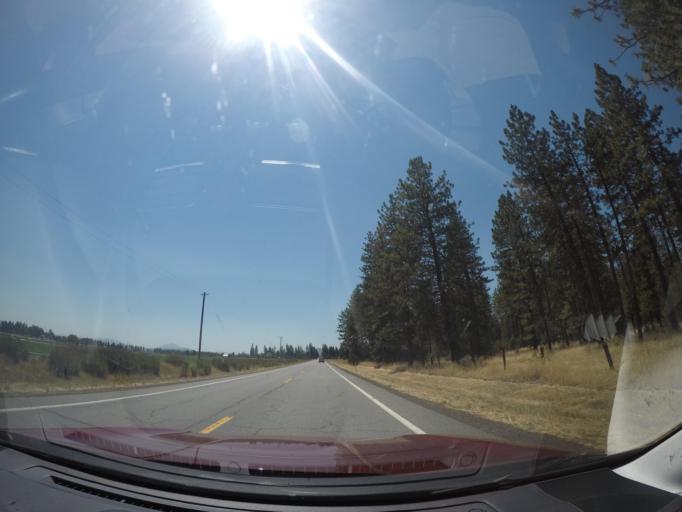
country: US
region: California
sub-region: Shasta County
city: Burney
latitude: 41.0706
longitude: -121.3389
